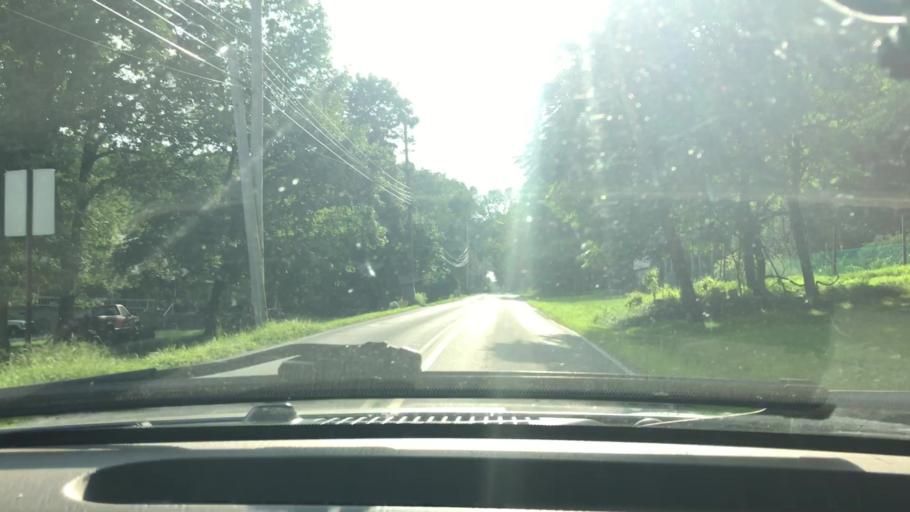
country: US
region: Pennsylvania
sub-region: Dauphin County
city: Hershey
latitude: 40.2209
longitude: -76.6396
